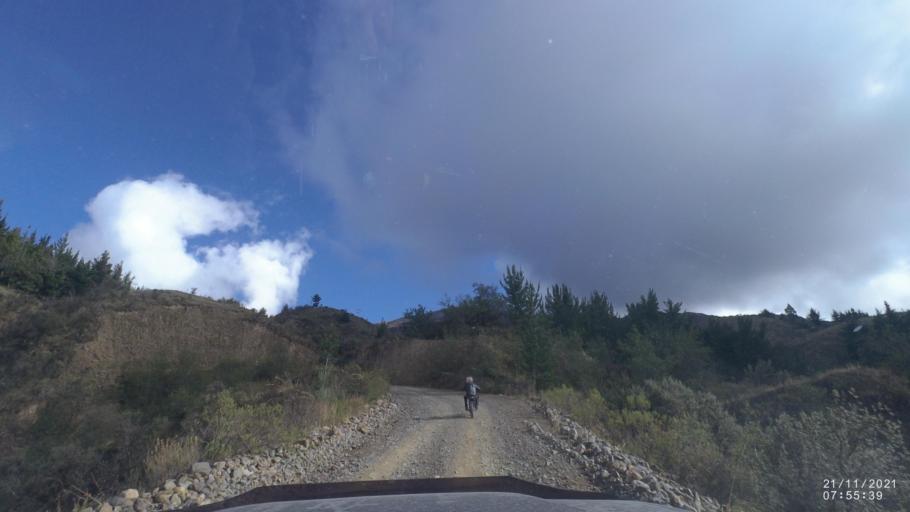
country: BO
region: Cochabamba
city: Cochabamba
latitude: -17.2992
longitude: -66.2180
